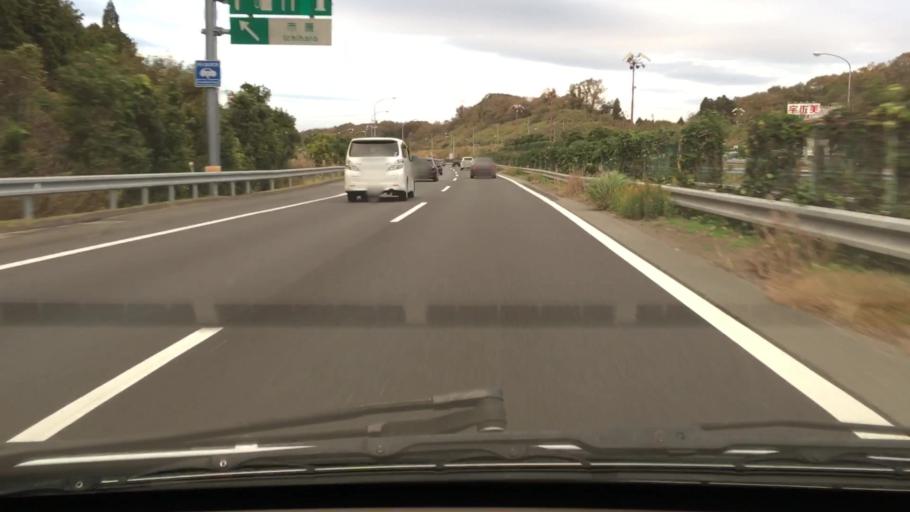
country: JP
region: Chiba
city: Ichihara
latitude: 35.4573
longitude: 140.0845
